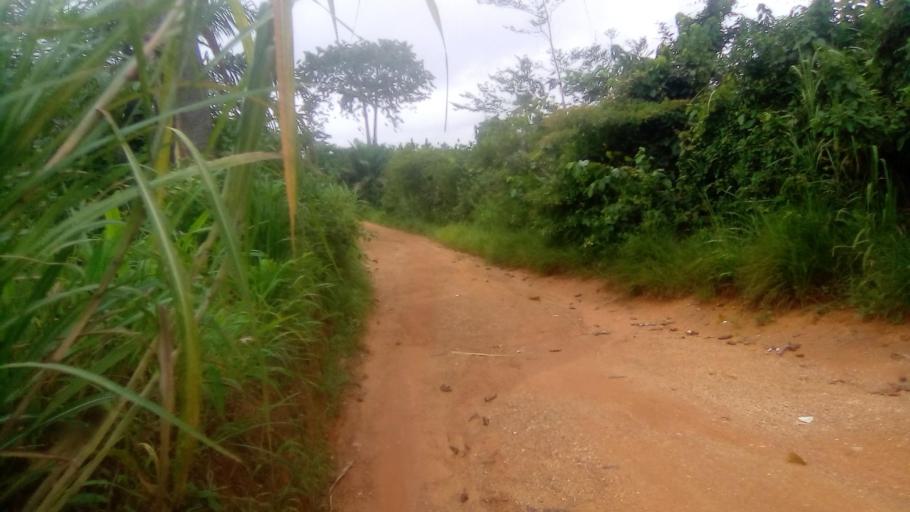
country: SL
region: Eastern Province
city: Kailahun
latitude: 8.3026
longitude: -10.5594
